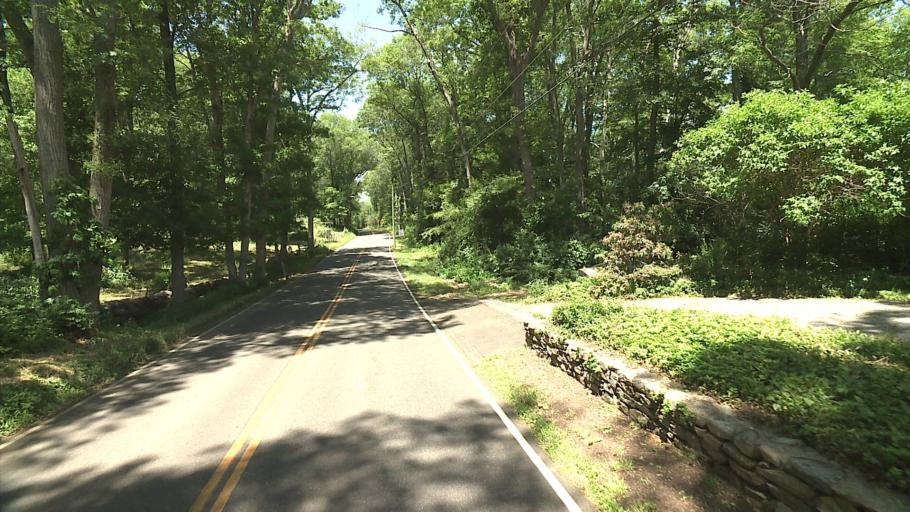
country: US
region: Rhode Island
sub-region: Washington County
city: Hopkinton
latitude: 41.4513
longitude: -71.8101
